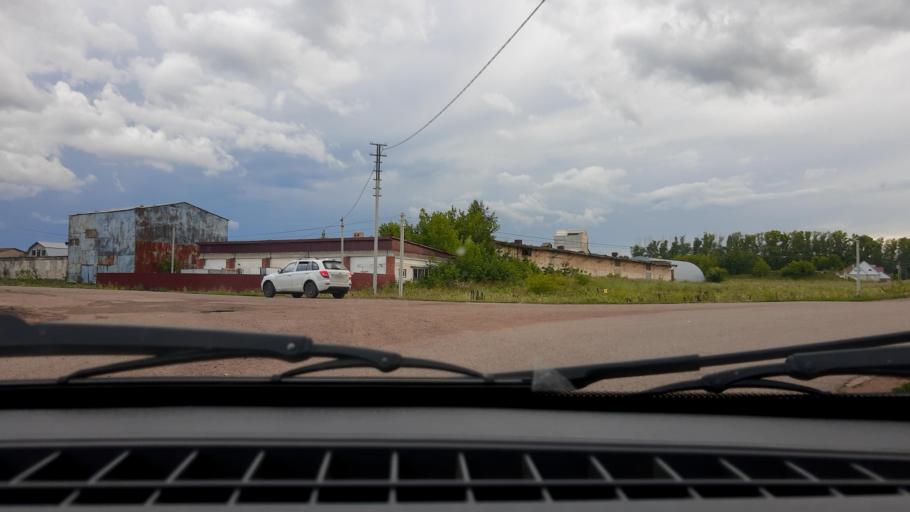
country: RU
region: Bashkortostan
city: Mikhaylovka
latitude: 54.8623
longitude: 55.8153
